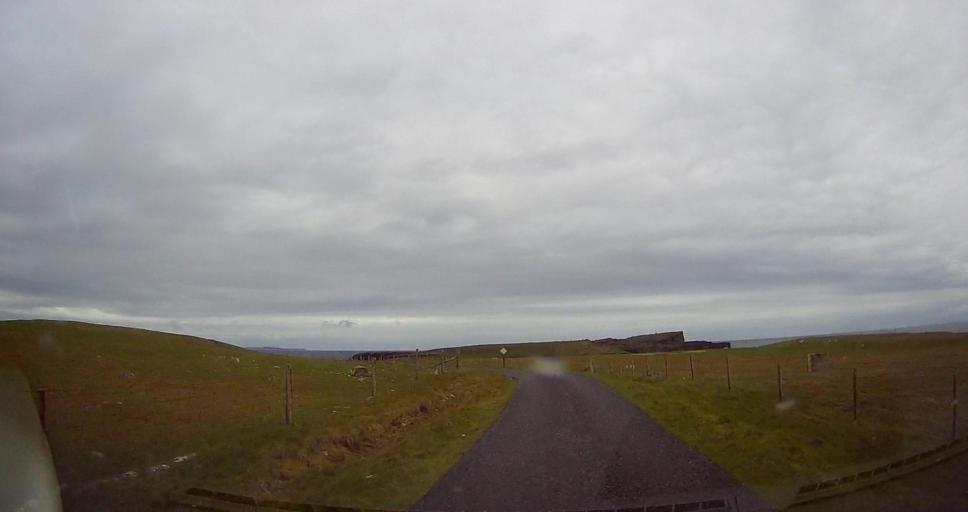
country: GB
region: Scotland
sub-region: Shetland Islands
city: Lerwick
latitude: 60.4801
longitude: -1.6116
